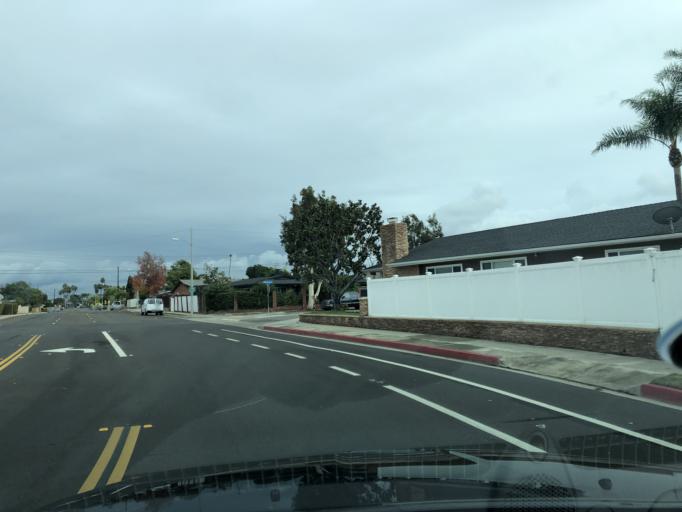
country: US
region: California
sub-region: Orange County
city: Fountain Valley
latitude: 33.6892
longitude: -117.9319
